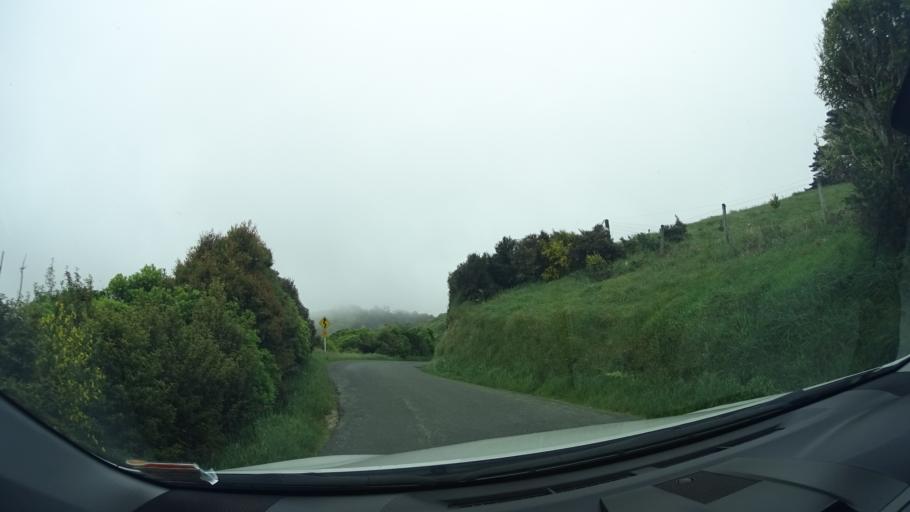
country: NZ
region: Wellington
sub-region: Wellington City
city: Brooklyn
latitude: -41.3053
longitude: 174.7495
